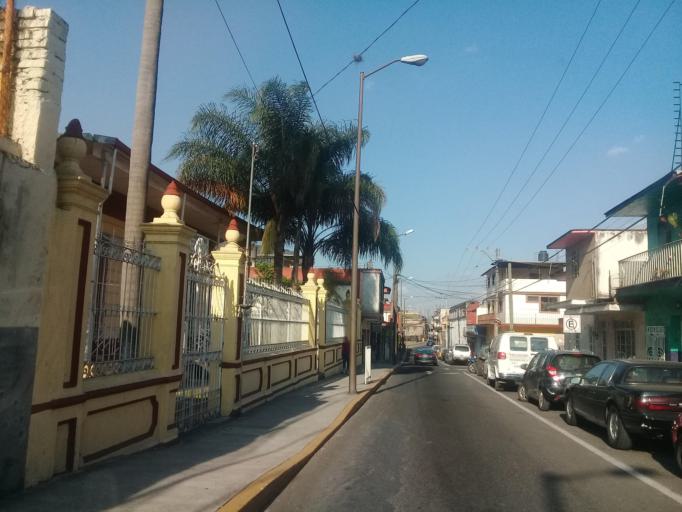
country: MX
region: Veracruz
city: Orizaba
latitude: 18.8490
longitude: -97.1092
